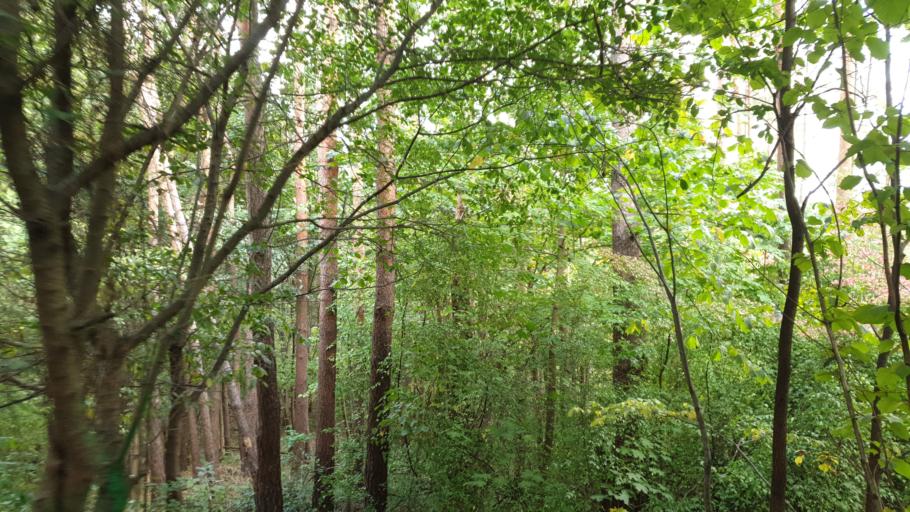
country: LT
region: Vilnius County
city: Seskine
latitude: 54.6930
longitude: 25.2320
